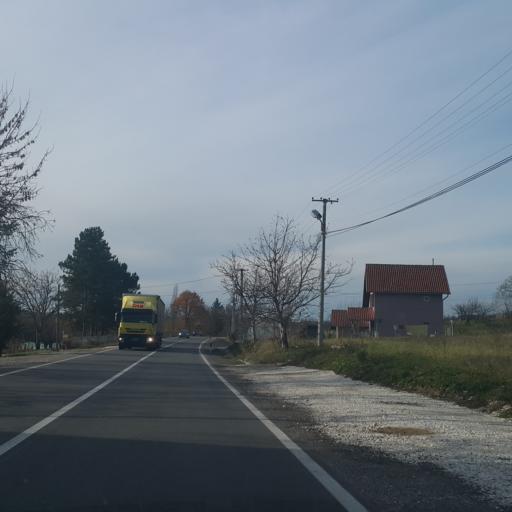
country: RS
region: Central Serbia
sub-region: Sumadijski Okrug
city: Arangelovac
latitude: 44.3394
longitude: 20.4217
